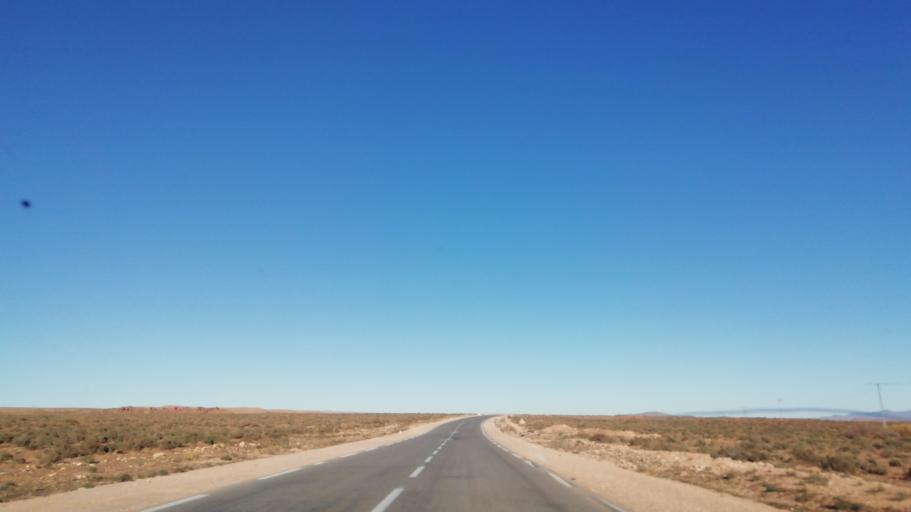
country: DZ
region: El Bayadh
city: El Abiodh Sidi Cheikh
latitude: 33.1313
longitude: 0.2896
